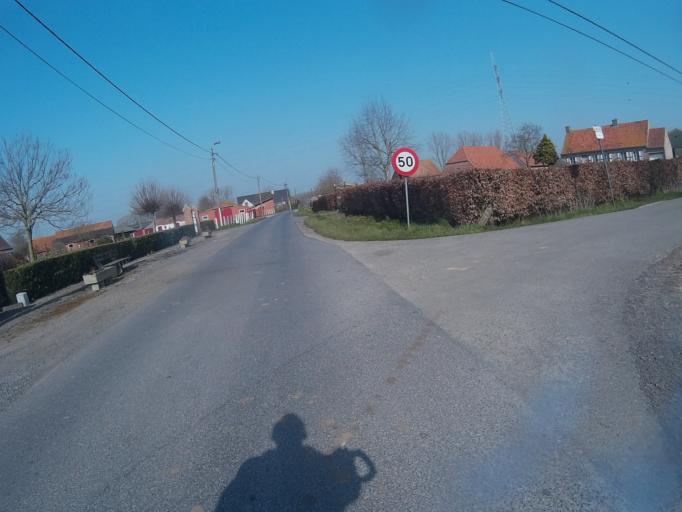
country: BE
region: Flanders
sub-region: Provincie Oost-Vlaanderen
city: Zomergem
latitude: 51.1143
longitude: 3.5174
